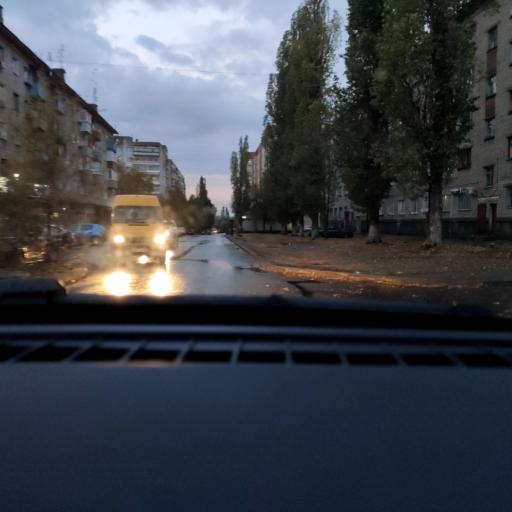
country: RU
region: Voronezj
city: Maslovka
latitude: 51.6116
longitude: 39.2324
